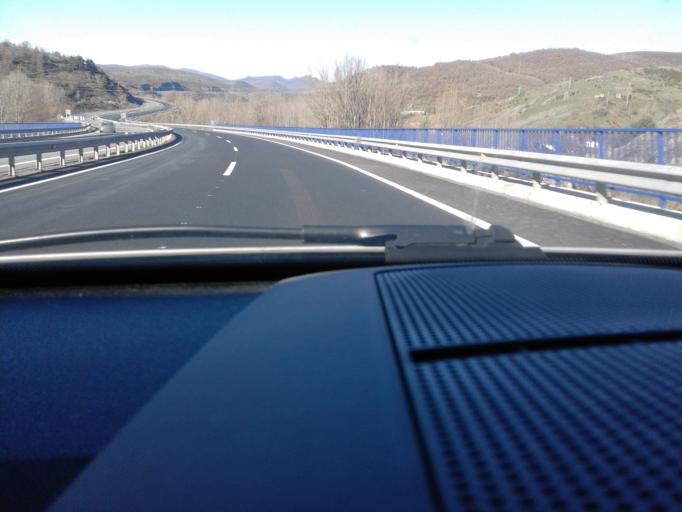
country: ES
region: Castille and Leon
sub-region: Provincia de Leon
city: Carrocera
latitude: 42.7867
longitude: -5.8042
